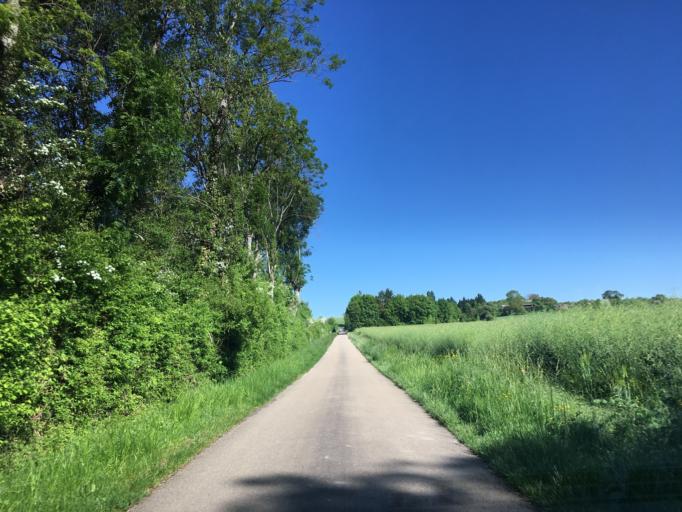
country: FR
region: Bourgogne
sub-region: Departement de l'Yonne
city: Aillant-sur-Tholon
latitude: 47.8246
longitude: 3.3439
